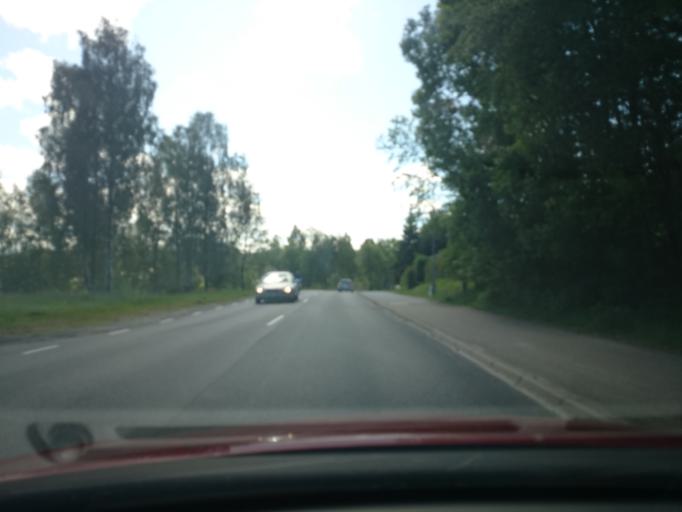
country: SE
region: Vaestra Goetaland
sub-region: Harryda Kommun
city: Landvetter
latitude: 57.6915
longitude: 12.2065
